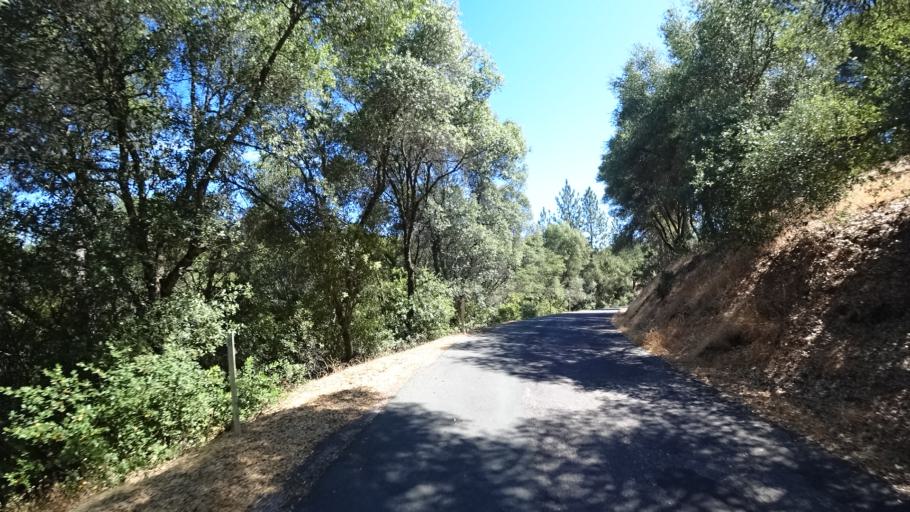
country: US
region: California
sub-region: Calaveras County
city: Angels Camp
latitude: 38.1462
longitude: -120.5518
